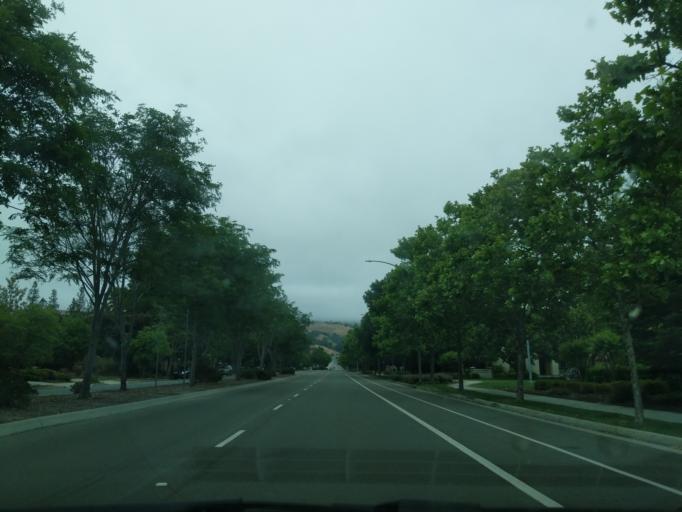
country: US
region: California
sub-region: Santa Clara County
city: Morgan Hill
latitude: 37.1365
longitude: -121.6203
